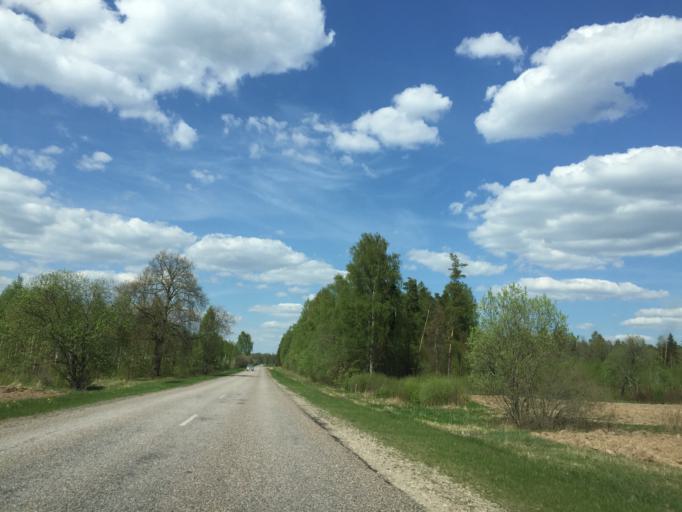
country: LV
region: Limbazu Rajons
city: Limbazi
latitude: 57.3904
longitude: 24.6895
